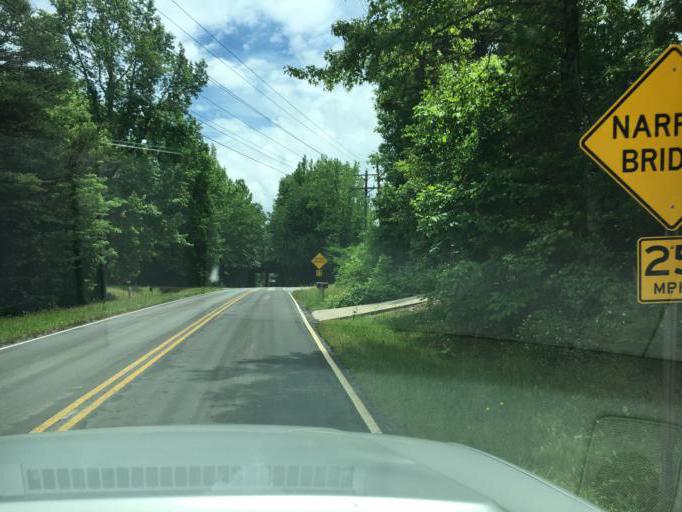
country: US
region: South Carolina
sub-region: Greenville County
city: Five Forks
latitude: 34.8515
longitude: -82.2796
